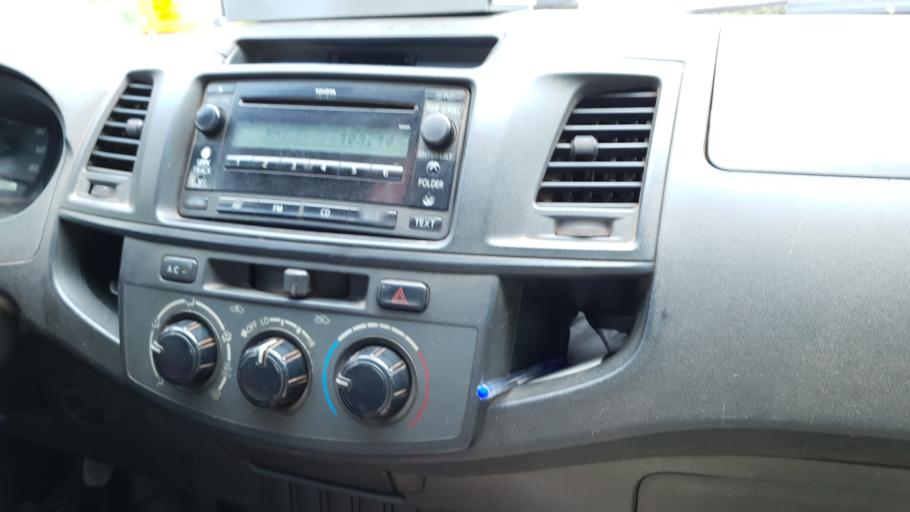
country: ML
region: Segou
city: Baroueli
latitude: 13.3531
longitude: -7.0963
